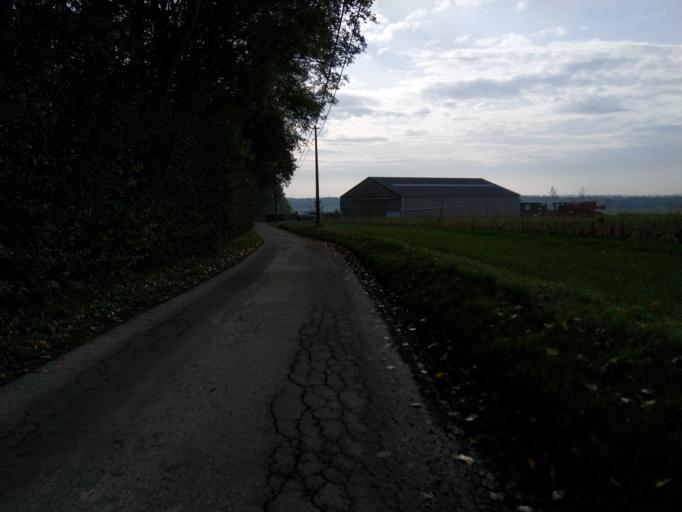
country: BE
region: Wallonia
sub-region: Province du Hainaut
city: Brugelette
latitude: 50.6093
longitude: 3.8780
